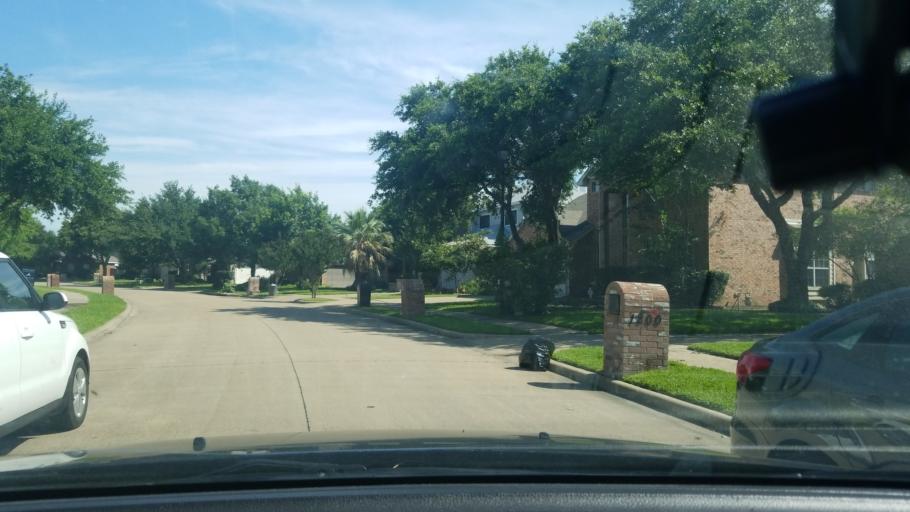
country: US
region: Texas
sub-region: Dallas County
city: Mesquite
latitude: 32.7785
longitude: -96.5832
